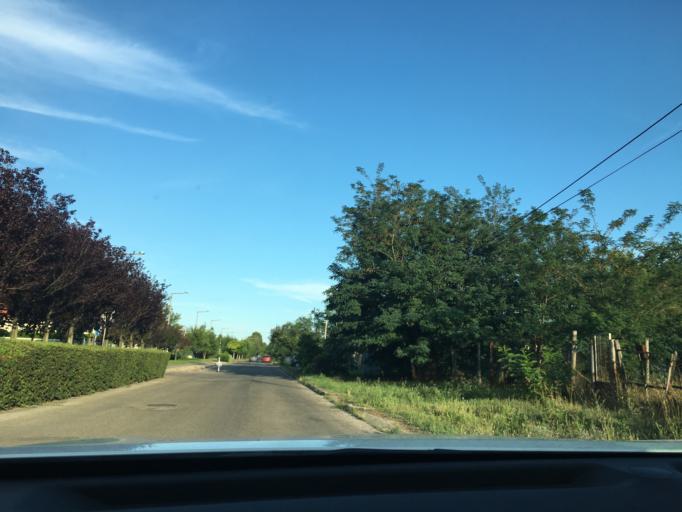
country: HU
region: Budapest
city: Budapest XVII. keruelet
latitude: 47.4721
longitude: 19.2677
